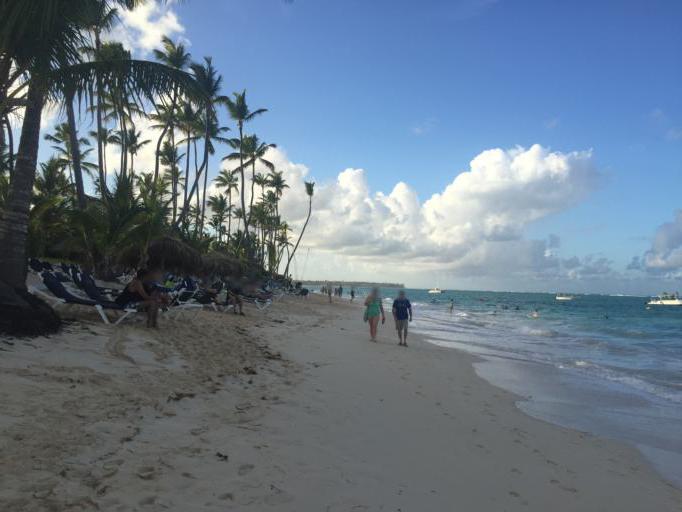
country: DO
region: San Juan
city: Punta Cana
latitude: 18.6946
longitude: -68.4259
